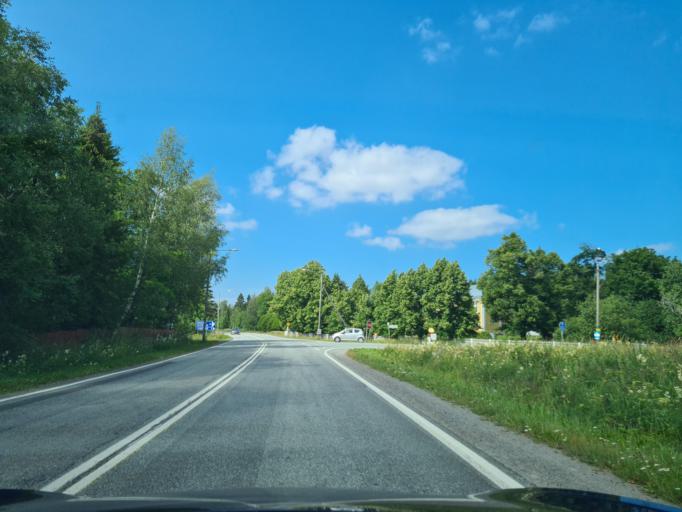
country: FI
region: Ostrobothnia
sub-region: Vaasa
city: Vaasa
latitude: 63.1919
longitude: 21.5617
